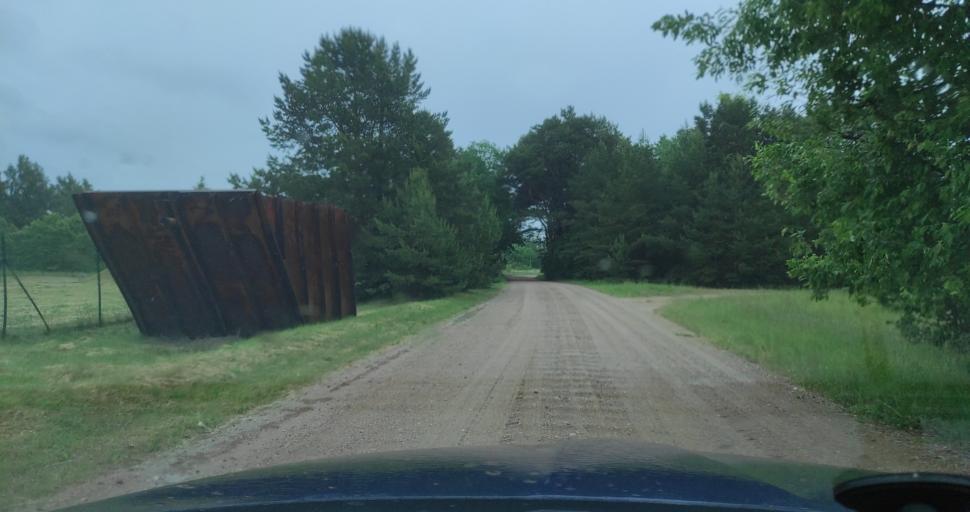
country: LV
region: Alsunga
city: Alsunga
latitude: 57.0012
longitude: 21.3902
